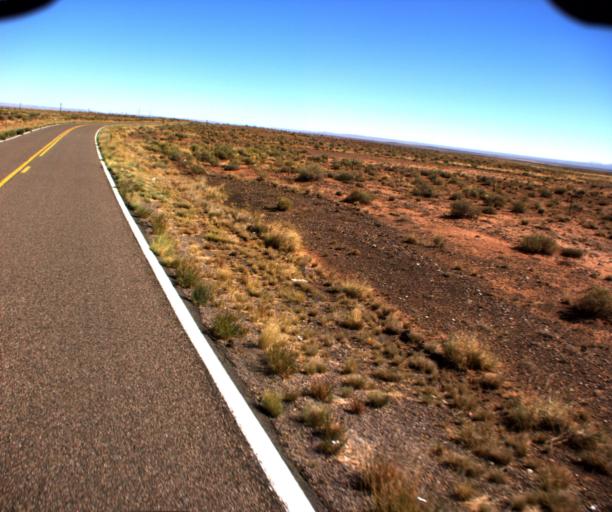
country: US
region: Arizona
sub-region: Coconino County
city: LeChee
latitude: 35.0918
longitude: -110.8606
